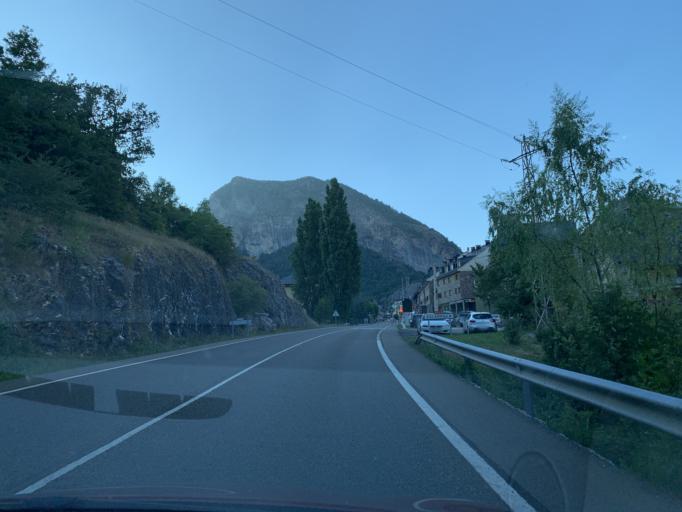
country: ES
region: Aragon
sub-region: Provincia de Huesca
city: Hoz de Jaca
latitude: 42.7309
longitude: -0.3102
